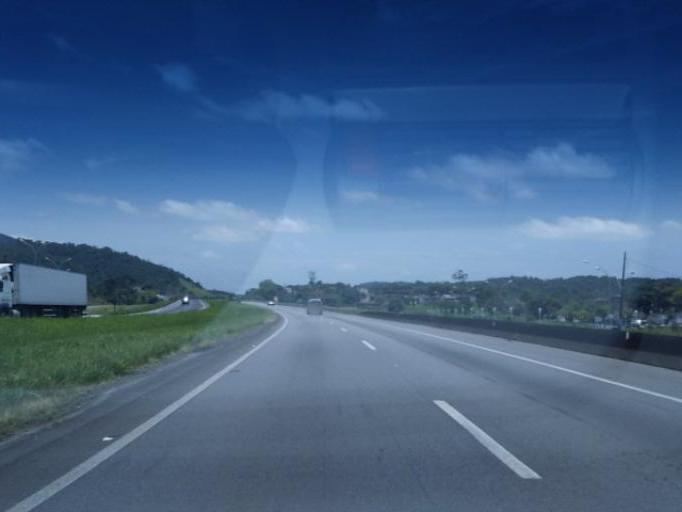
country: BR
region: Sao Paulo
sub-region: Miracatu
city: Miracatu
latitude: -24.2877
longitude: -47.4577
